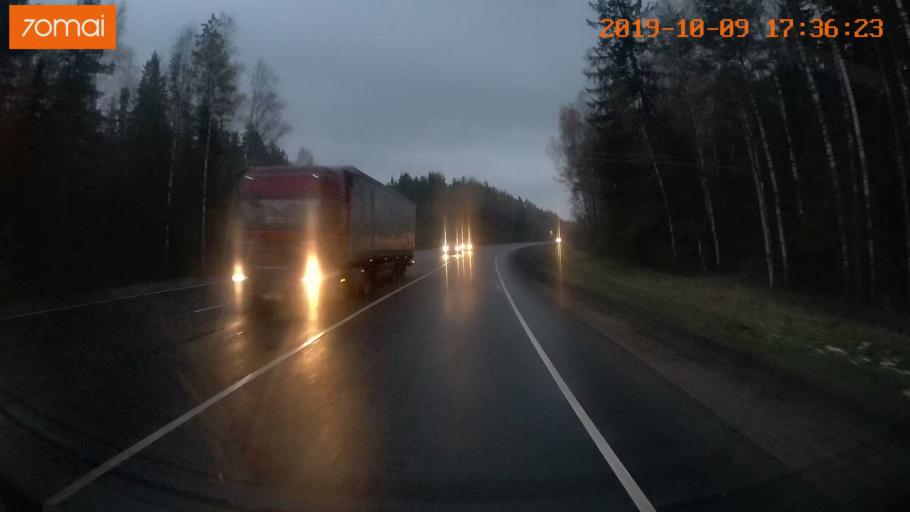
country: RU
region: Ivanovo
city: Bogorodskoye
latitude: 57.0792
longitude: 40.9977
